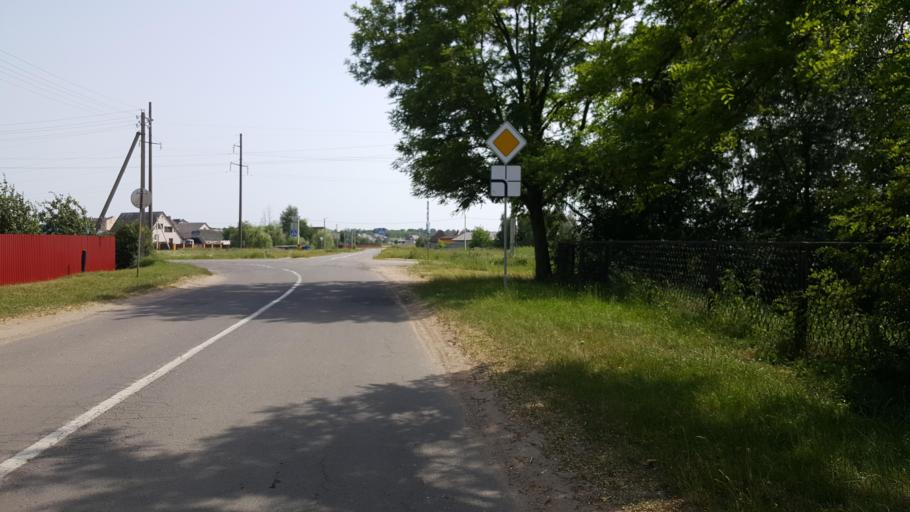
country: BY
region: Brest
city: Kamyanyets
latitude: 52.3951
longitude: 23.8127
